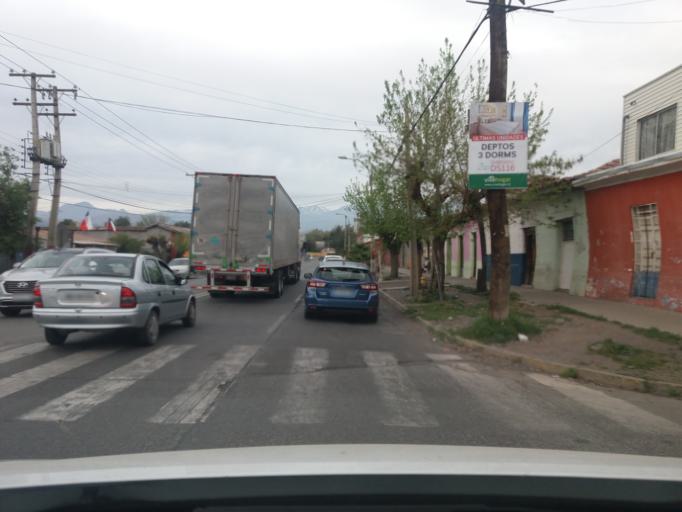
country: CL
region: Valparaiso
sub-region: Provincia de San Felipe
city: San Felipe
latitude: -32.7566
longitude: -70.7344
